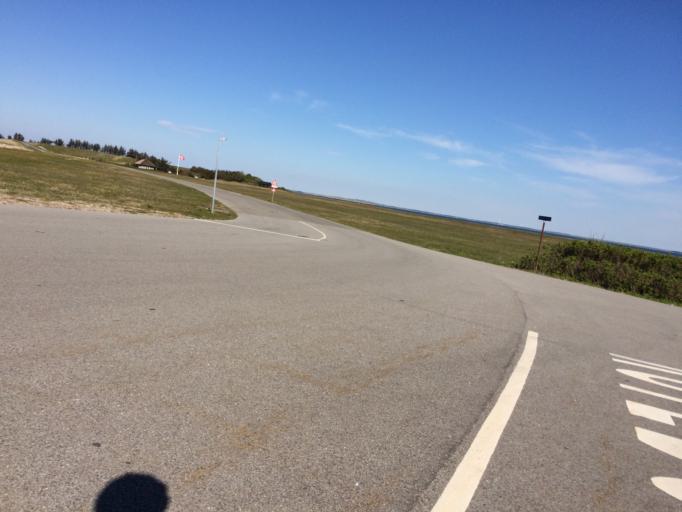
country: DK
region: Central Jutland
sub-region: Struer Kommune
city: Struer
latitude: 56.5158
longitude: 8.6179
